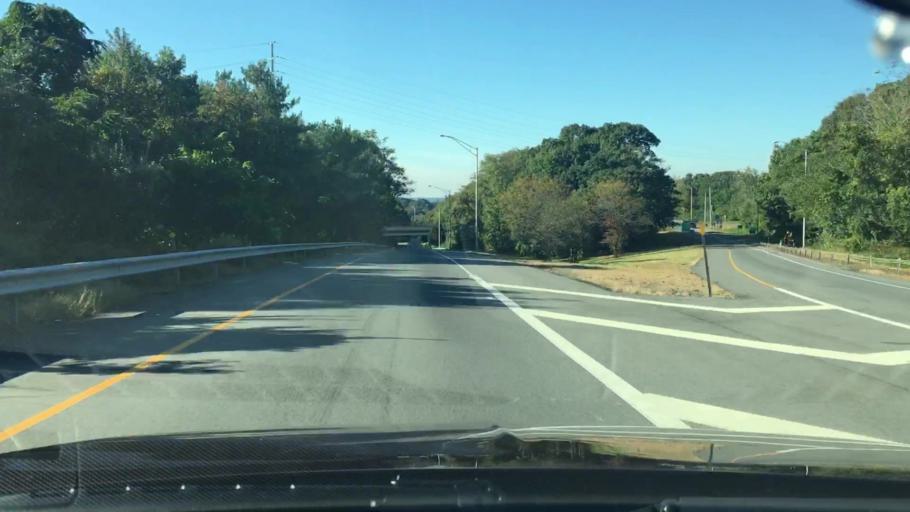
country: US
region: Connecticut
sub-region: Fairfield County
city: Trumbull
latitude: 41.2348
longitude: -73.1558
